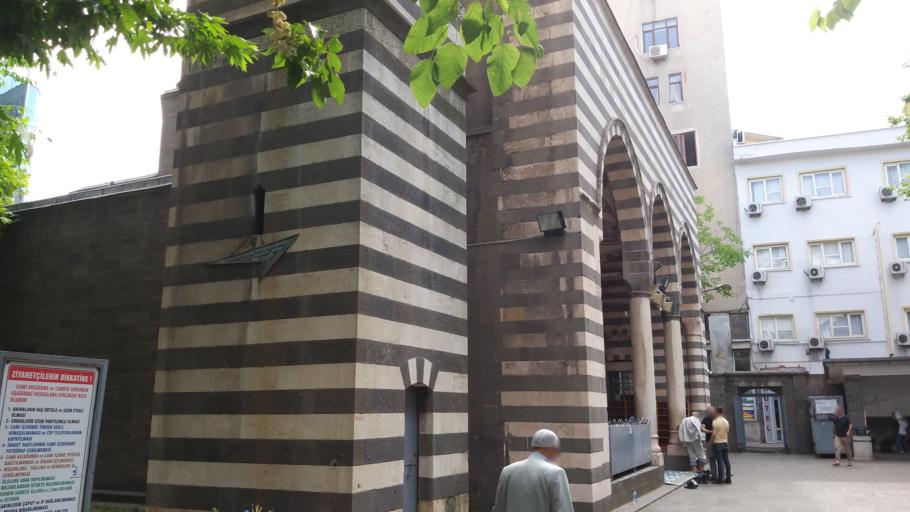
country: TR
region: Diyarbakir
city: Sur
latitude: 37.9152
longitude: 40.2367
